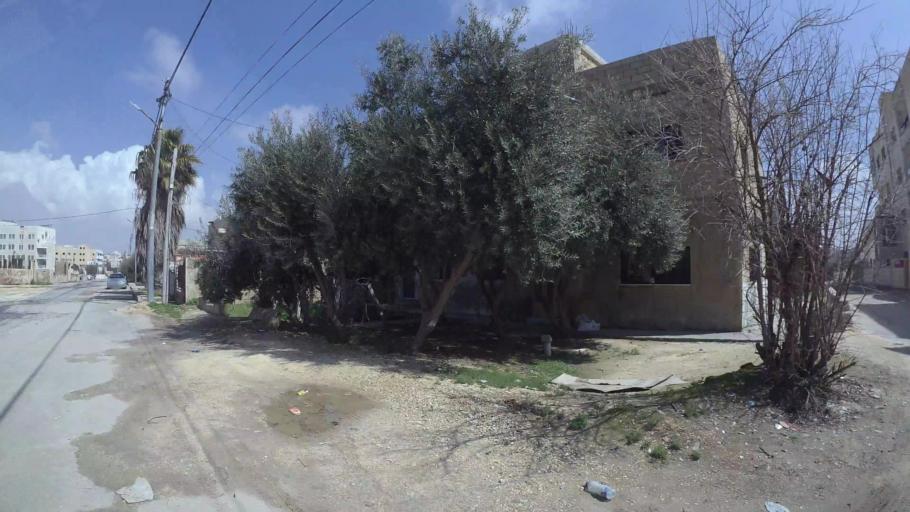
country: JO
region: Amman
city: Al Bunayyat ash Shamaliyah
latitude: 31.8978
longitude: 35.8931
